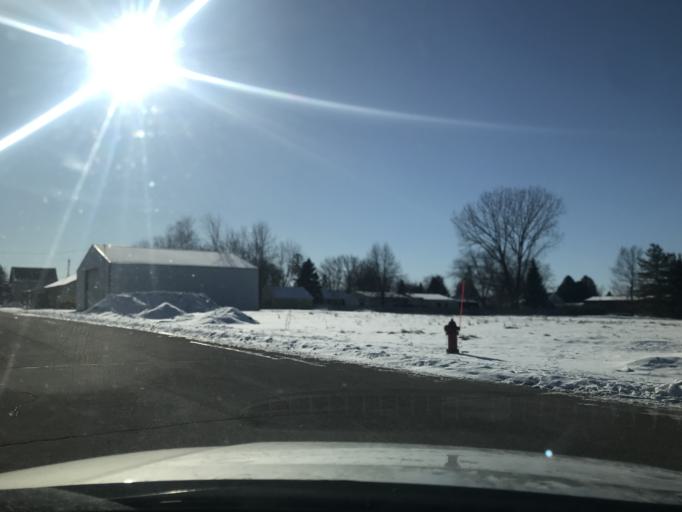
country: US
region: Wisconsin
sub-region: Oconto County
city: Oconto Falls
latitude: 44.9534
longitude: -88.0497
